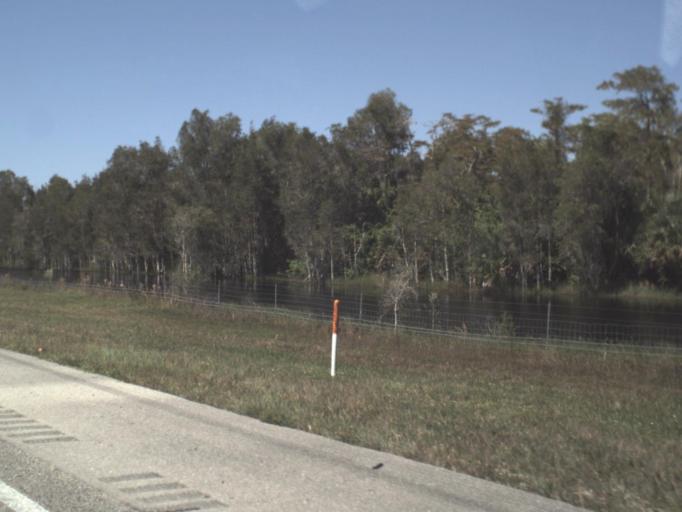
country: US
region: Florida
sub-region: Collier County
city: Golden Gate
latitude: 26.1540
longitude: -81.6050
